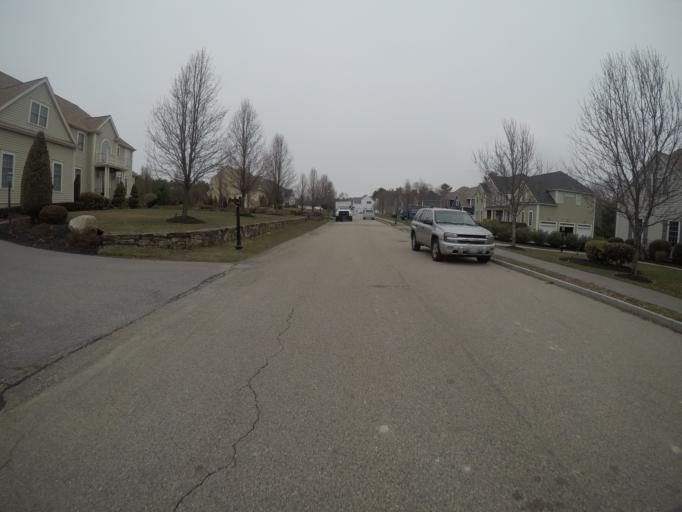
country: US
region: Massachusetts
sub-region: Bristol County
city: Easton
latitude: 42.0140
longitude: -71.1088
